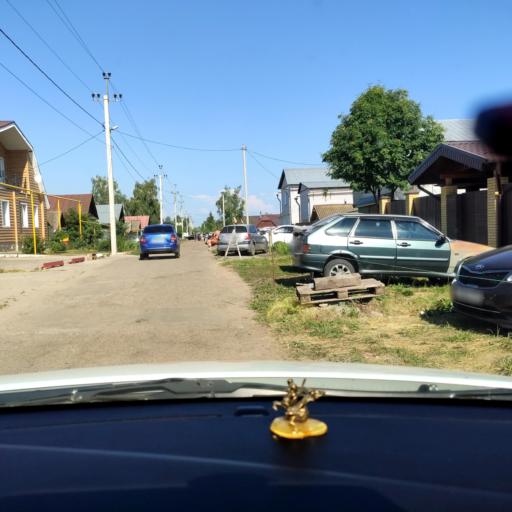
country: RU
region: Tatarstan
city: Laishevo
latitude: 55.3969
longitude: 49.5461
